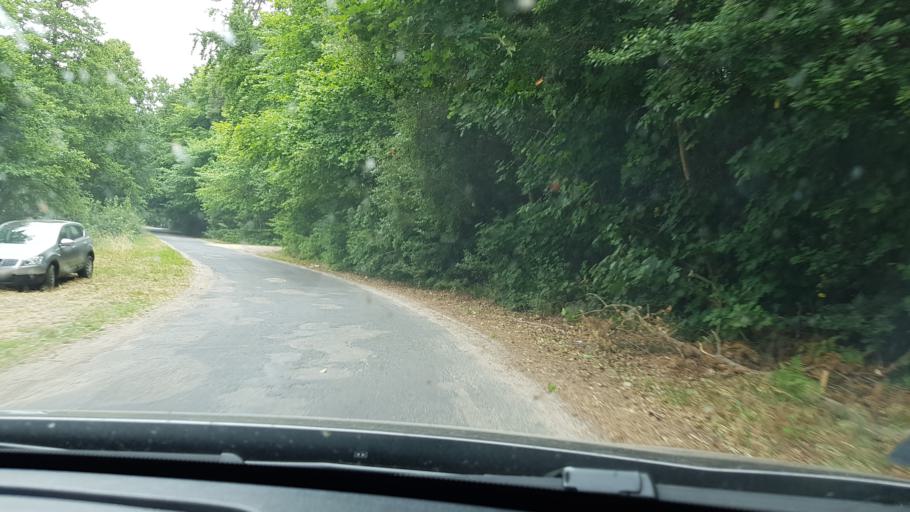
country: PL
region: West Pomeranian Voivodeship
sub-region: Powiat kamienski
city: Miedzyzdroje
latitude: 53.9606
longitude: 14.5692
